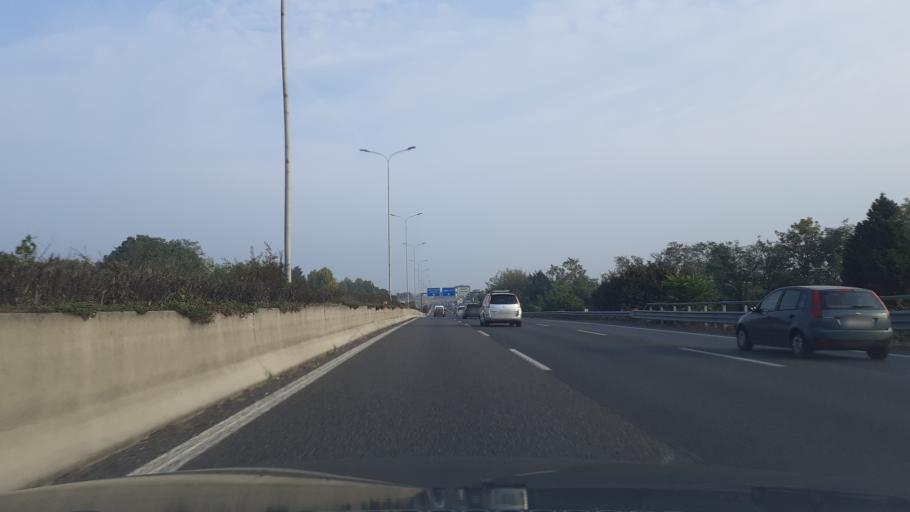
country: IT
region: Lombardy
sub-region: Provincia di Monza e Brianza
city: Santa Margherita
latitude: 45.6424
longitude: 9.2255
